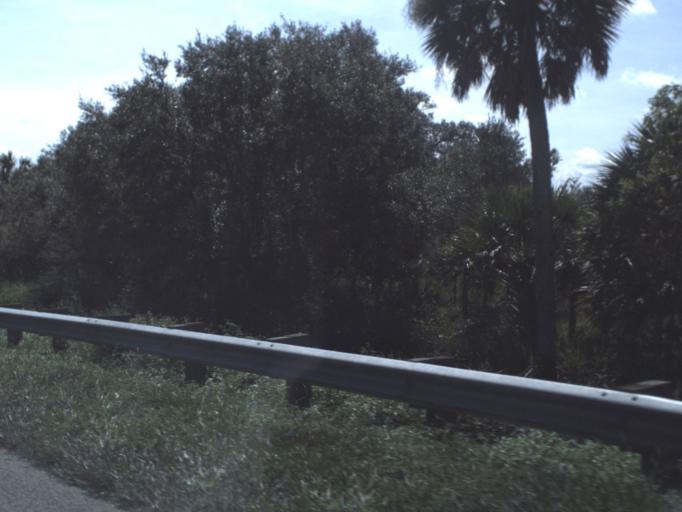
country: US
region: Florida
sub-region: Glades County
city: Moore Haven
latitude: 26.8856
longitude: -81.2315
